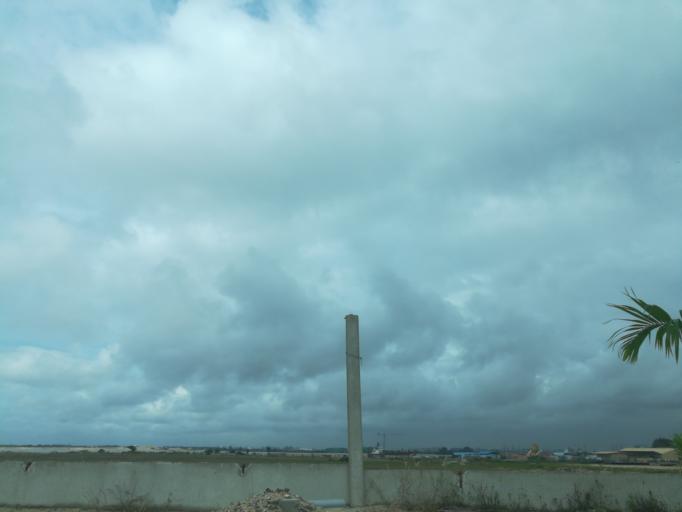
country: NG
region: Lagos
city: Lagos
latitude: 6.4160
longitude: 3.4121
